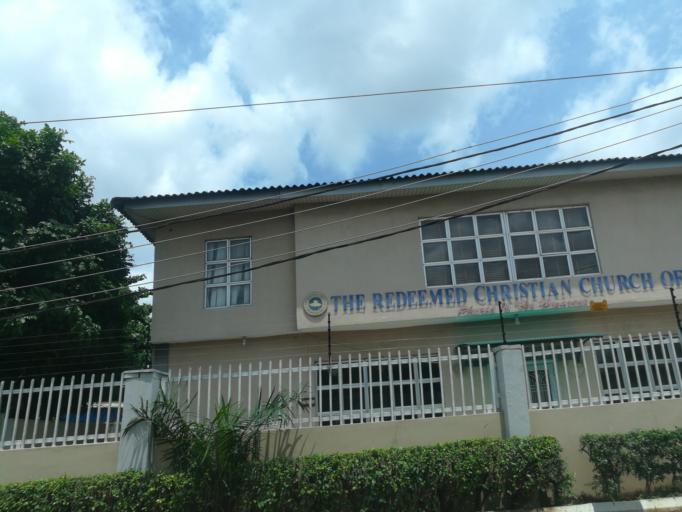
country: NG
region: Lagos
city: Somolu
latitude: 6.5435
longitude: 3.3625
